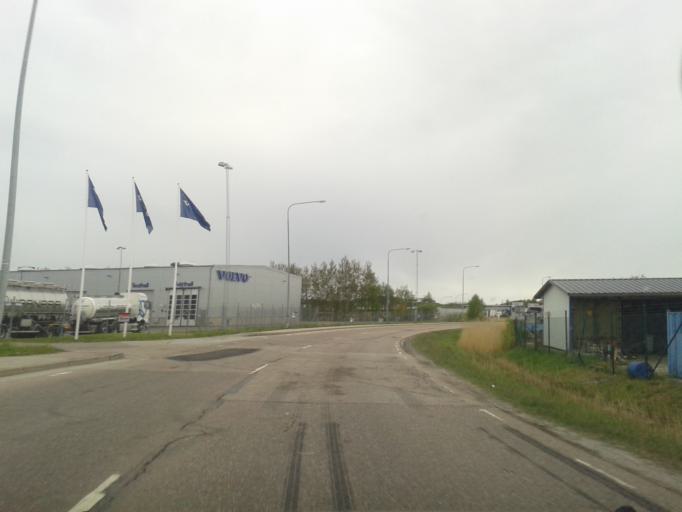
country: SE
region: Vaestra Goetaland
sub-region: Stenungsunds Kommun
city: Stora Hoga
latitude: 58.0215
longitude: 11.8413
